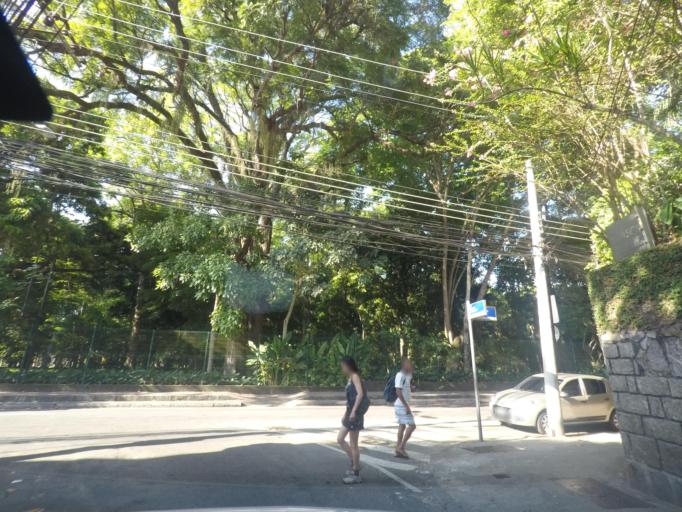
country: BR
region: Rio de Janeiro
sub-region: Rio De Janeiro
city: Rio de Janeiro
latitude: -22.9659
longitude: -43.2205
